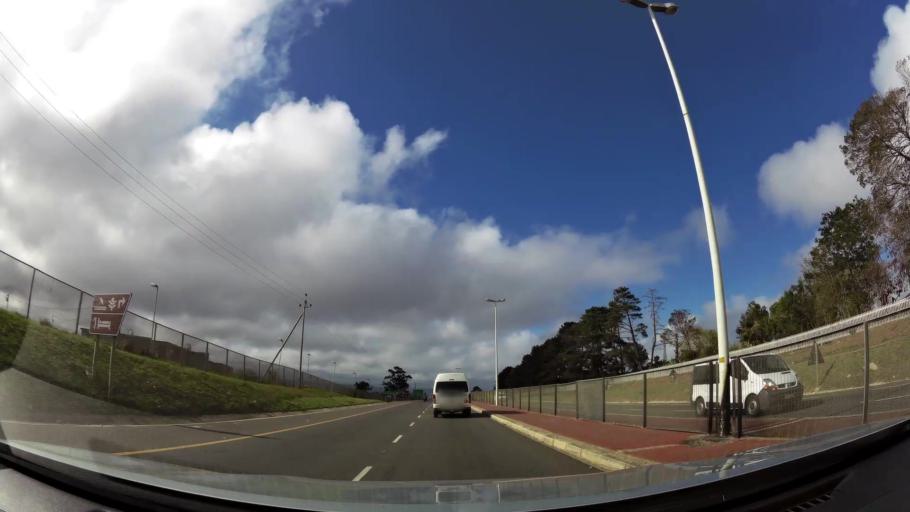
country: ZA
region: Western Cape
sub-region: Eden District Municipality
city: Plettenberg Bay
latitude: -34.0524
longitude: 23.3506
